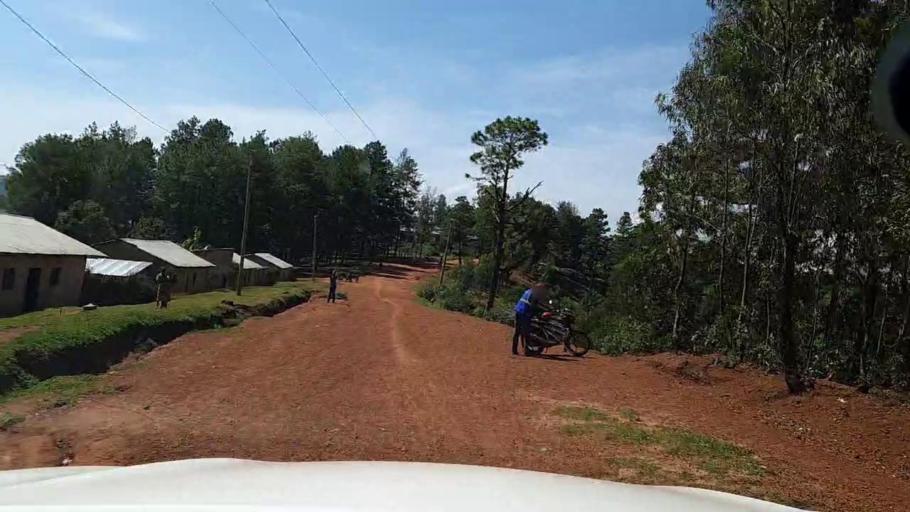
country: RW
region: Southern Province
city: Butare
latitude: -2.7155
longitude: 29.8394
